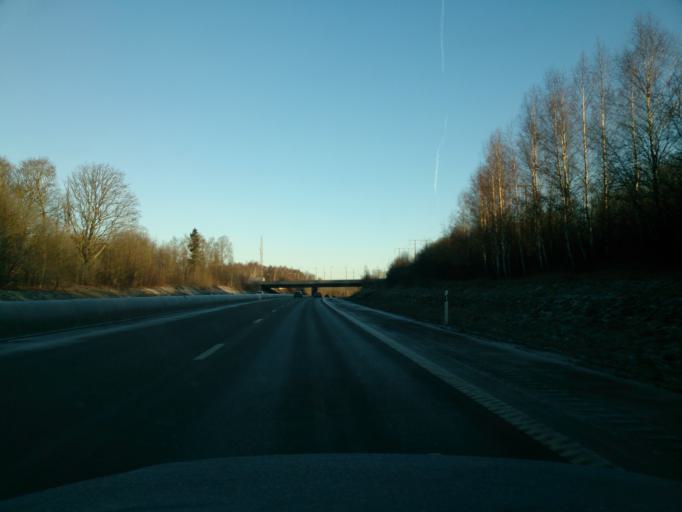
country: SE
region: OEstergoetland
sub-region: Norrkopings Kommun
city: Norrkoping
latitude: 58.6082
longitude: 16.1317
